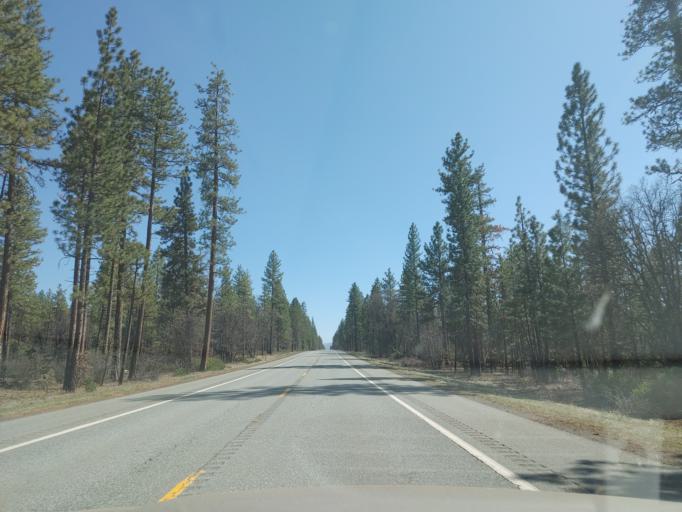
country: US
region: California
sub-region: Shasta County
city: Burney
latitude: 40.9761
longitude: -121.6215
